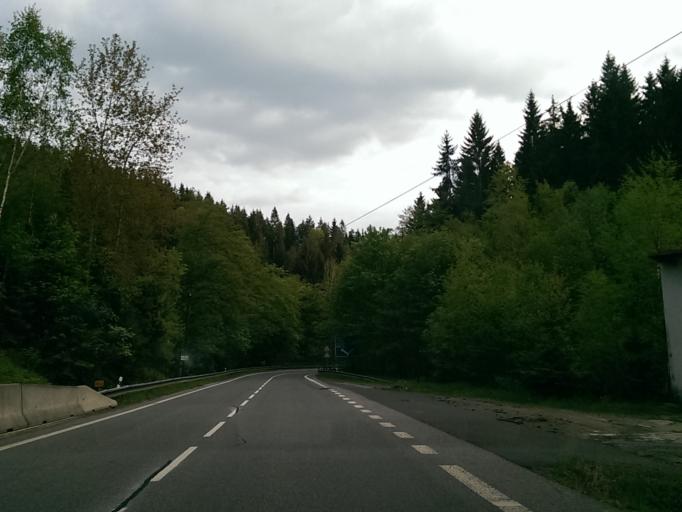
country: CZ
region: Liberecky
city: Zelezny Brod
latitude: 50.6735
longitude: 15.2675
